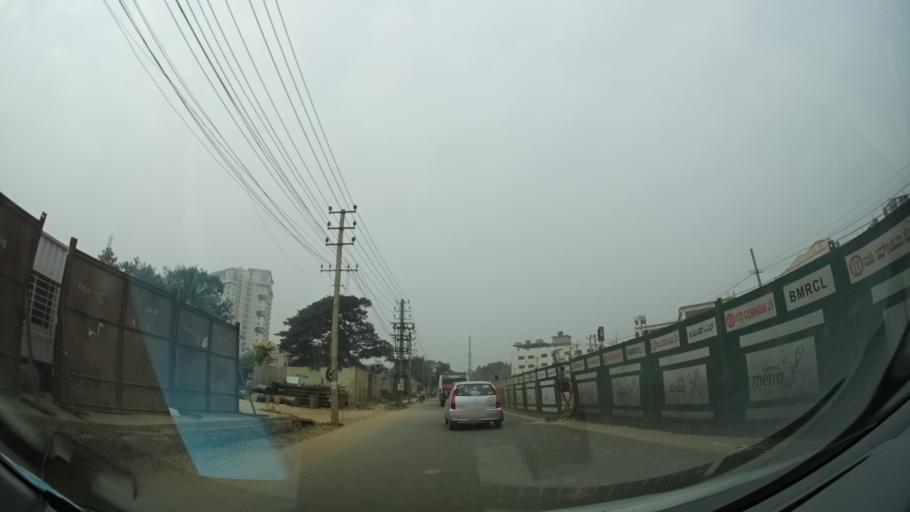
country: IN
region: Karnataka
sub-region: Bangalore Rural
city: Hoskote
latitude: 12.9890
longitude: 77.7118
